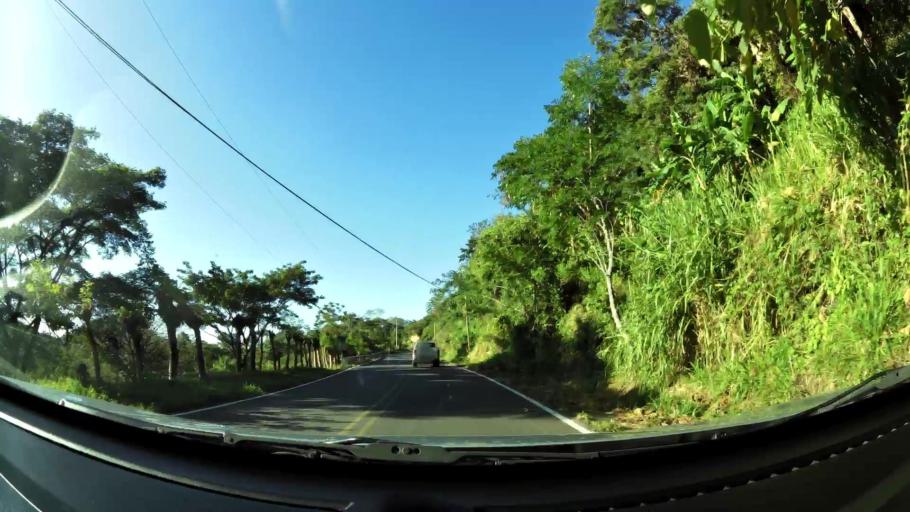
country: CR
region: Guanacaste
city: Juntas
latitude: 10.2162
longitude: -84.8525
